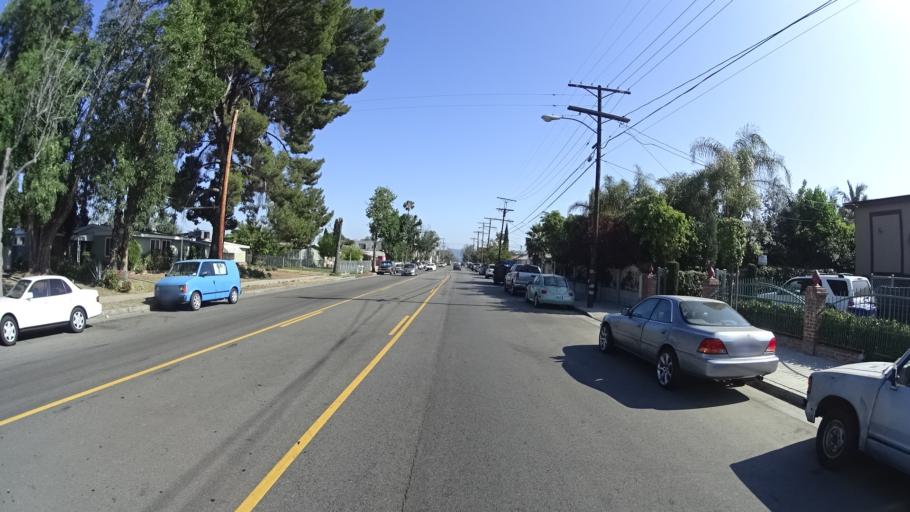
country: US
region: California
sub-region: Los Angeles County
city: Van Nuys
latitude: 34.1892
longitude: -118.4225
